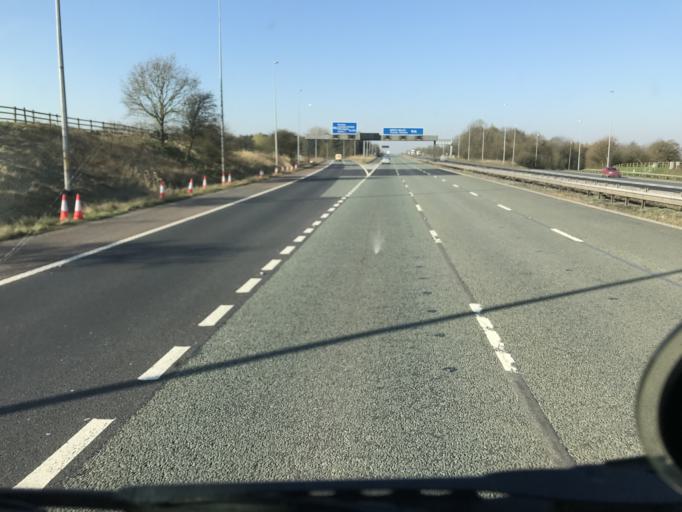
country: GB
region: England
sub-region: Warrington
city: Lymm
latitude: 53.3550
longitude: -2.4931
